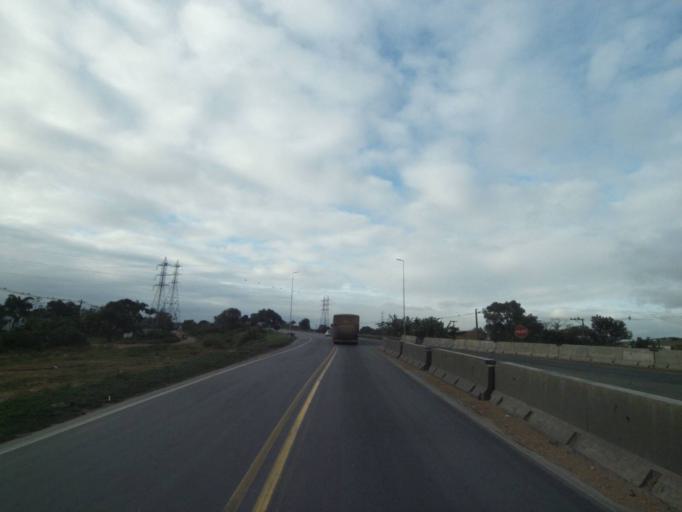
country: BR
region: Parana
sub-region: Paranagua
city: Paranagua
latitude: -25.5545
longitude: -48.5630
